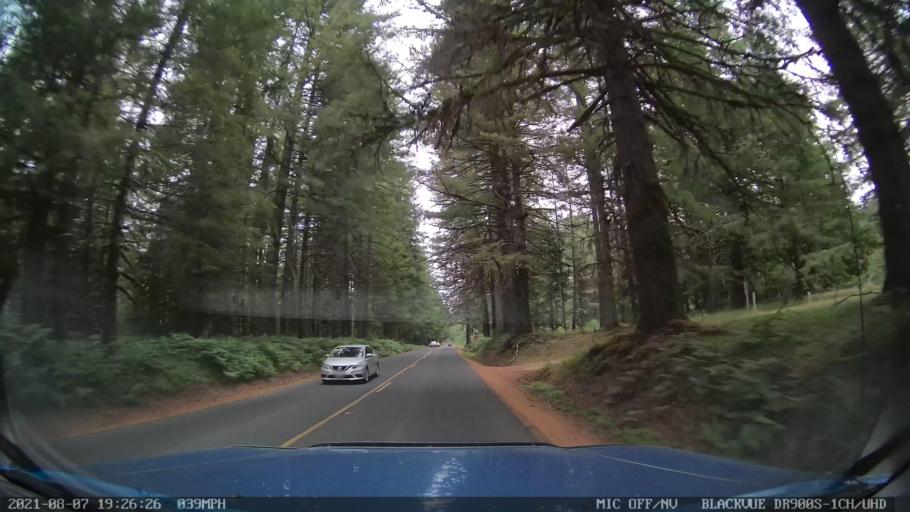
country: US
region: Oregon
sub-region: Linn County
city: Lyons
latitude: 44.8718
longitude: -122.6517
